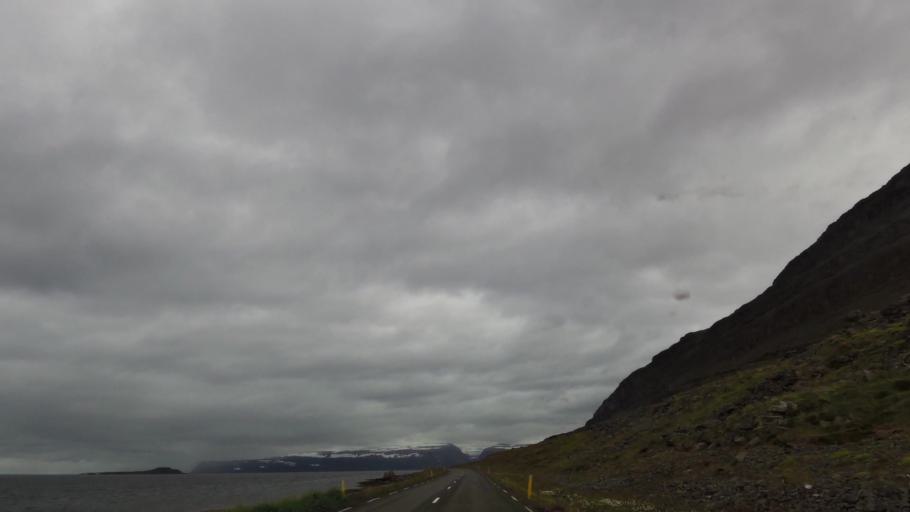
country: IS
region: Westfjords
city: Isafjoerdur
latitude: 66.0129
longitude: -22.7818
